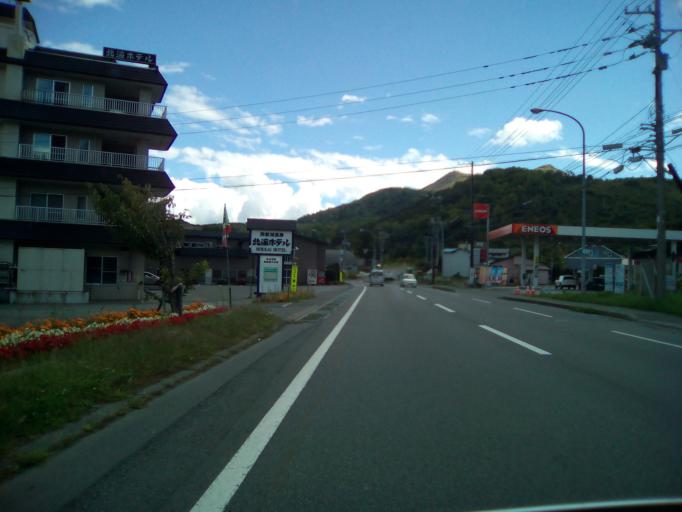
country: JP
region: Hokkaido
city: Date
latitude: 42.5654
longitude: 140.8092
